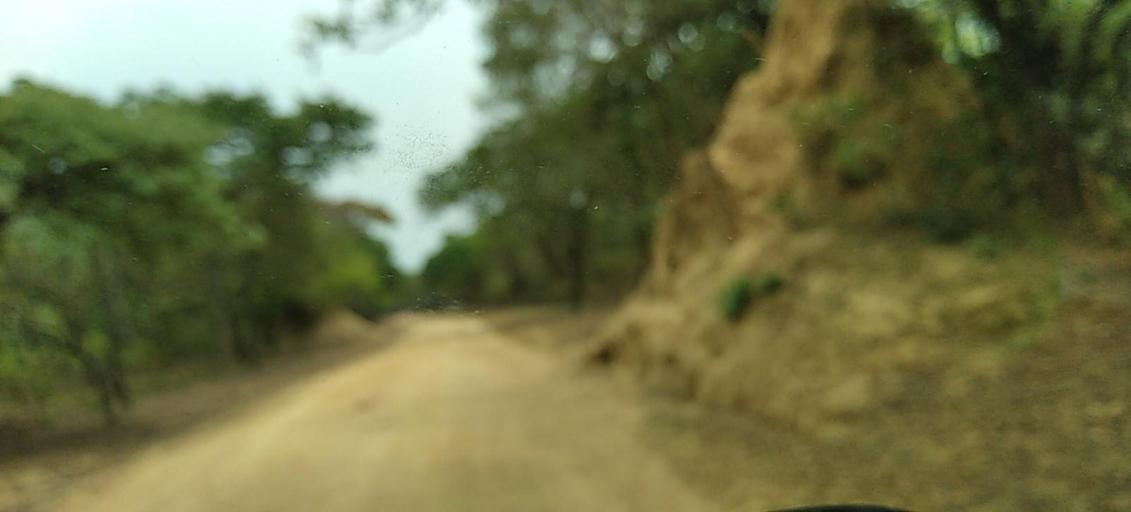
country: ZM
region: North-Western
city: Solwezi
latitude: -12.9331
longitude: 26.5596
